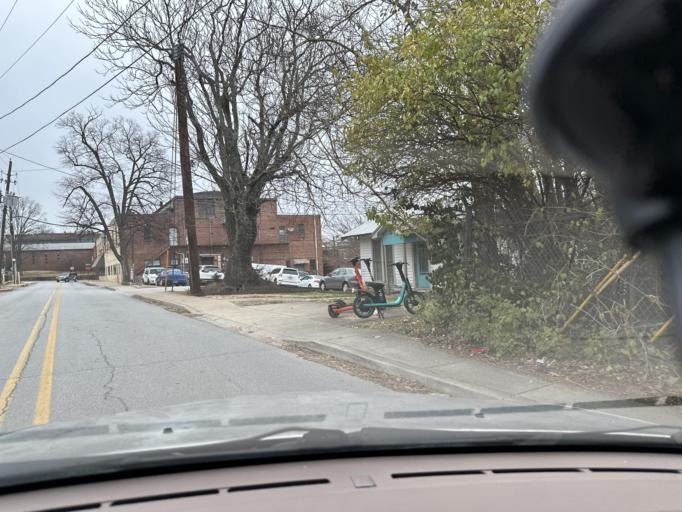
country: US
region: Arkansas
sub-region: Washington County
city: Fayetteville
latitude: 36.0655
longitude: -94.1696
